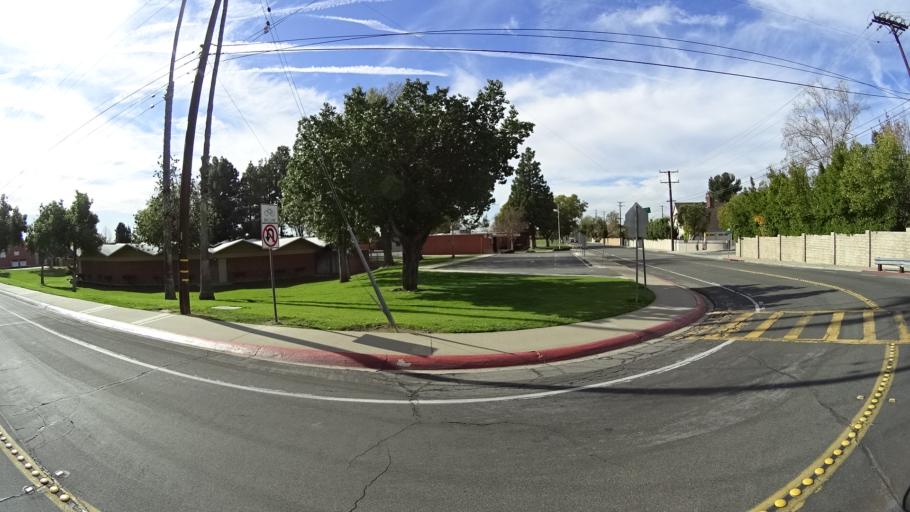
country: US
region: California
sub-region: Orange County
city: Villa Park
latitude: 33.8213
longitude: -117.8179
